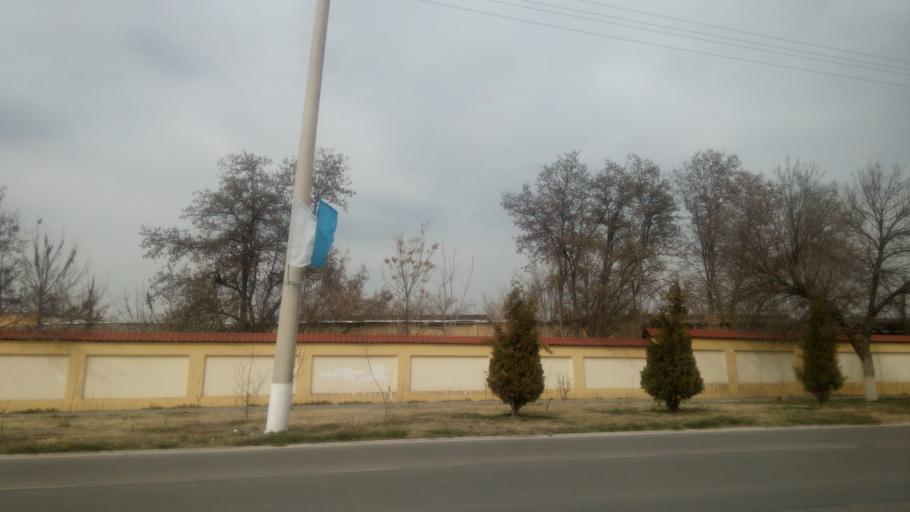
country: UZ
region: Toshkent
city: Salor
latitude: 41.3359
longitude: 69.3185
